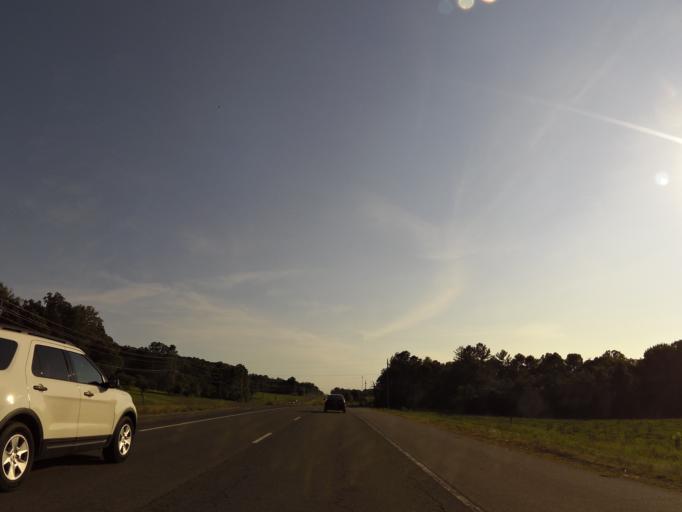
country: US
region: Tennessee
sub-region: Monroe County
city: Madisonville
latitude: 35.5509
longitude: -84.3137
